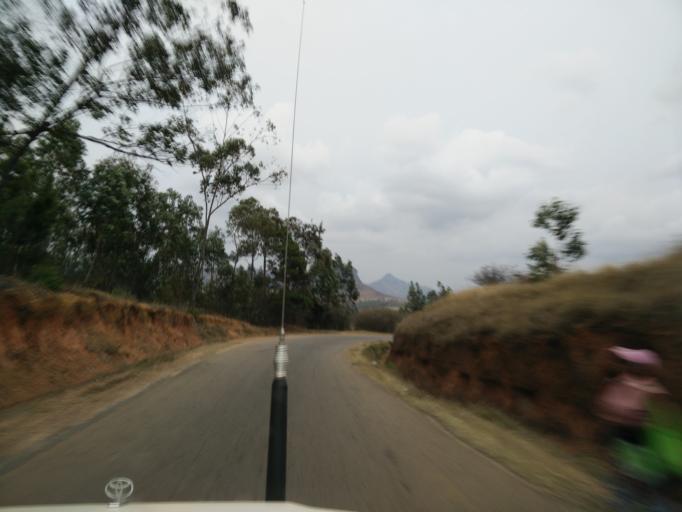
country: MG
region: Upper Matsiatra
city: Fianarantsoa
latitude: -21.5390
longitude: 47.0501
